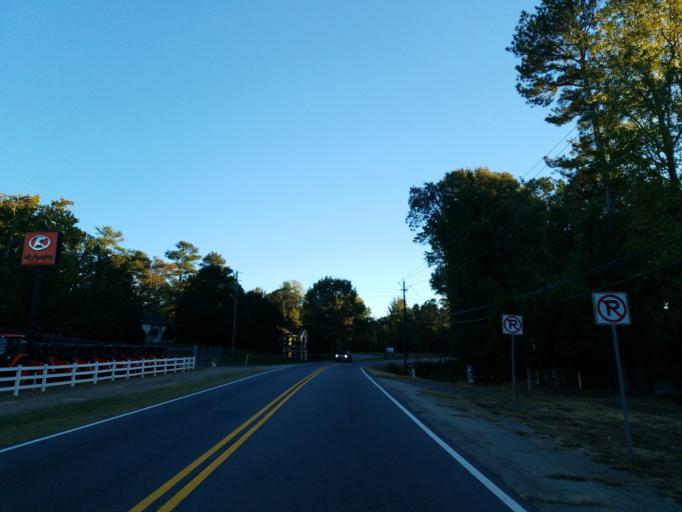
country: US
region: Georgia
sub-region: Forsyth County
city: Cumming
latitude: 34.2574
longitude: -84.1050
